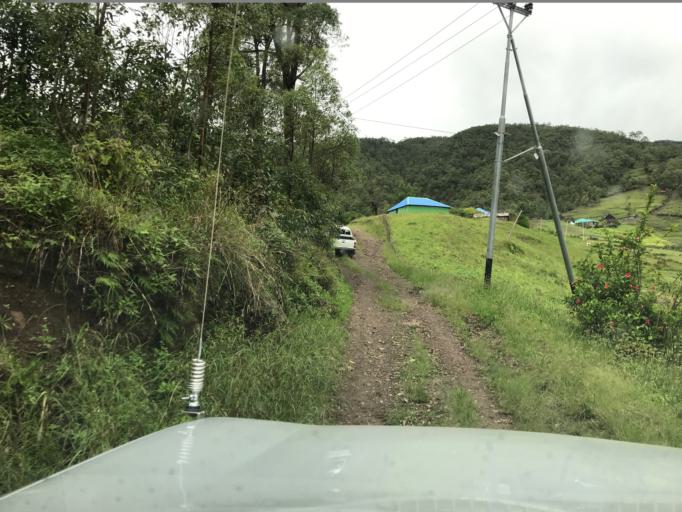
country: TL
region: Ainaro
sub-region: Ainaro
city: Ainaro
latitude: -8.8671
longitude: 125.5538
